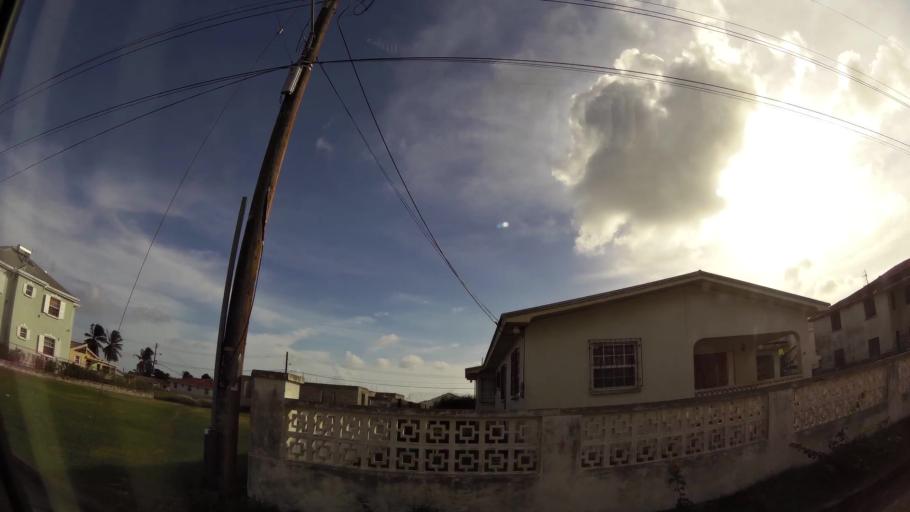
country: BB
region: Christ Church
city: Oistins
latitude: 13.0817
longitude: -59.5661
